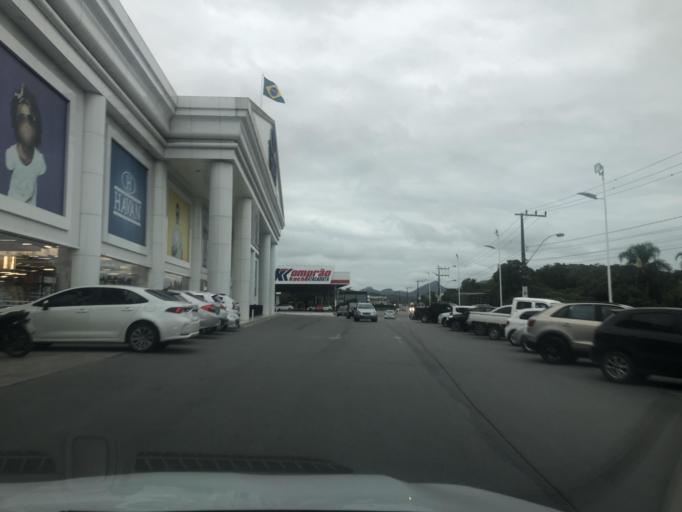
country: BR
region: Santa Catarina
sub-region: Sao Francisco Do Sul
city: Sao Francisco do Sul
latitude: -26.2530
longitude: -48.6185
